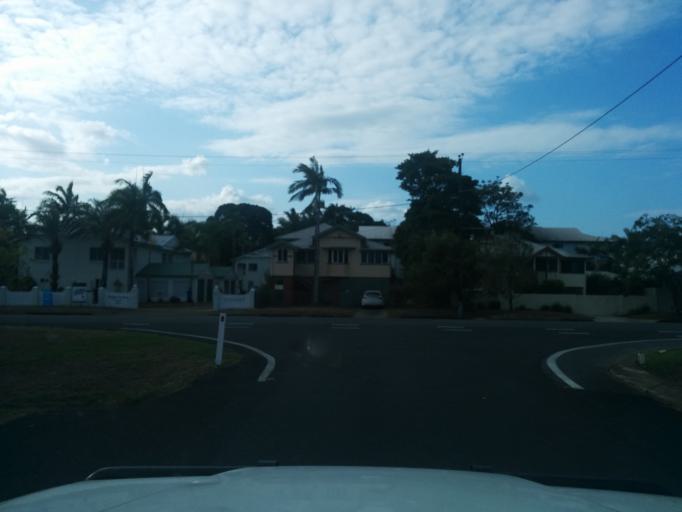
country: AU
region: Queensland
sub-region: Cairns
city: Cairns
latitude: -16.9166
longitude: 145.7590
